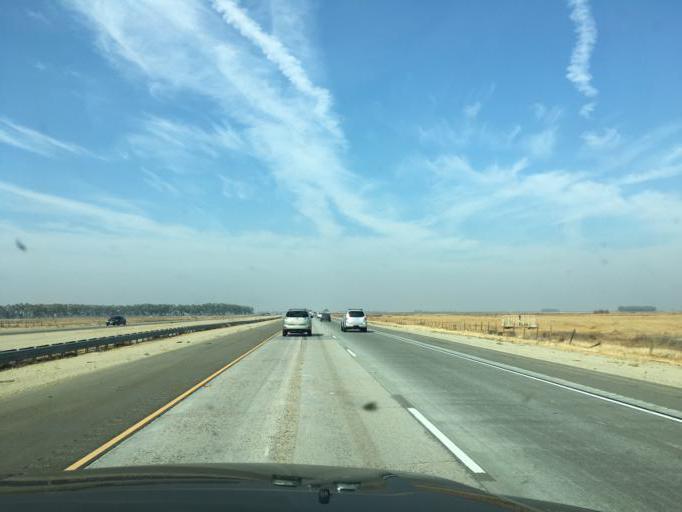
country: US
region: California
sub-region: Kern County
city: Lost Hills
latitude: 35.5605
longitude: -119.6005
